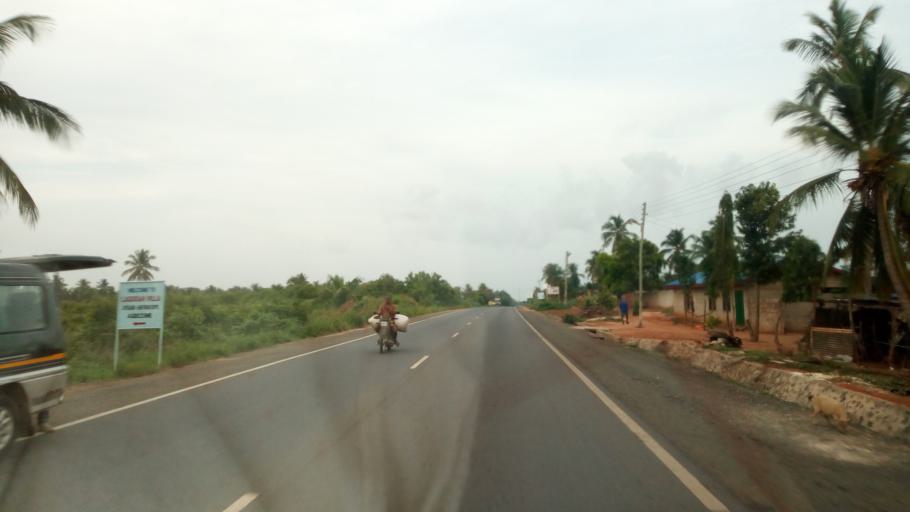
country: TG
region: Maritime
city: Lome
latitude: 6.0861
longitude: 1.0611
